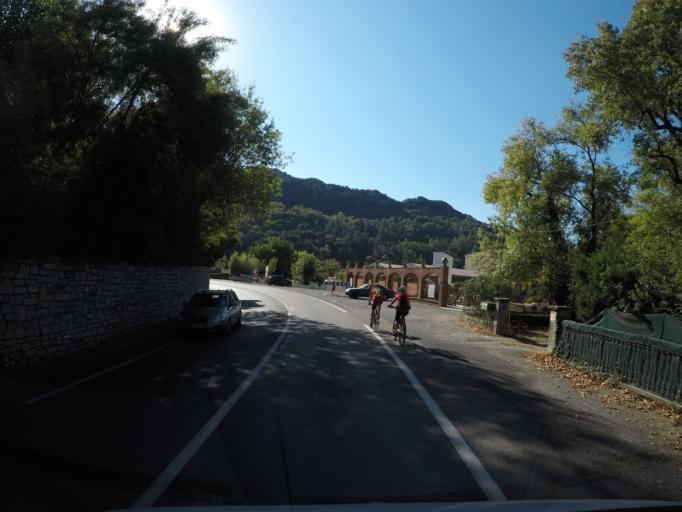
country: FR
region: Languedoc-Roussillon
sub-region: Departement du Gard
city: Anduze
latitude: 44.0592
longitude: 3.9741
